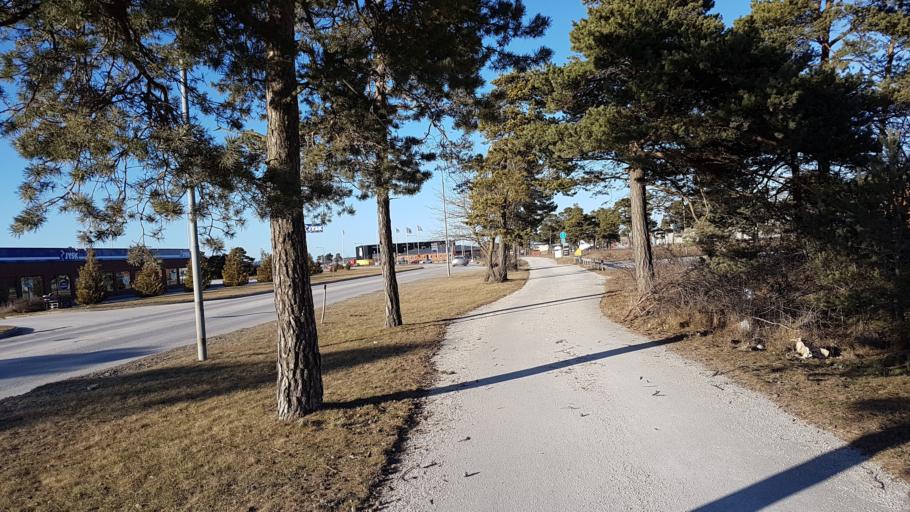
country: SE
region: Gotland
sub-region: Gotland
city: Visby
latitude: 57.6376
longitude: 18.3276
